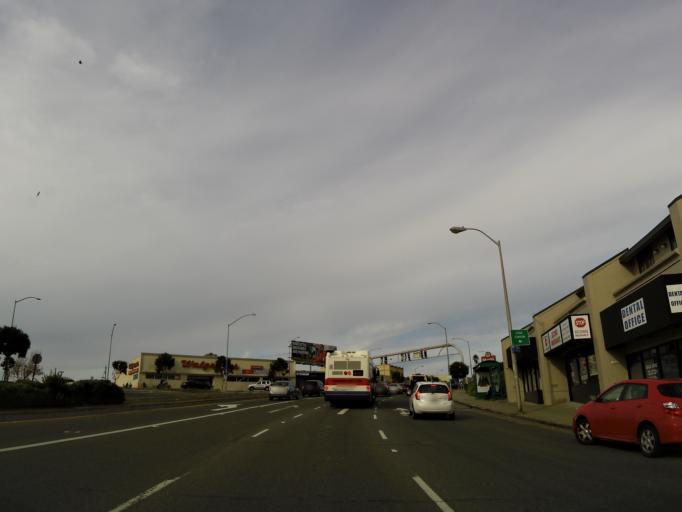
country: US
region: California
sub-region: San Mateo County
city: Colma
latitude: 37.6886
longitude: -122.4659
